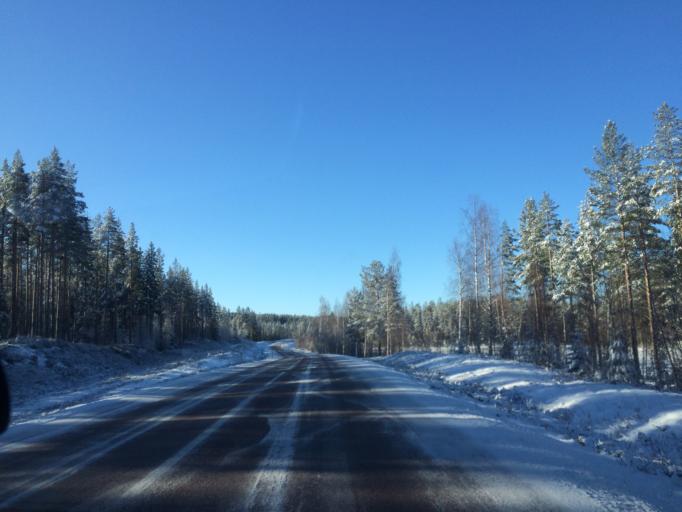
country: SE
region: Dalarna
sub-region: Mora Kommun
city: Mora
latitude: 60.8756
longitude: 14.3702
